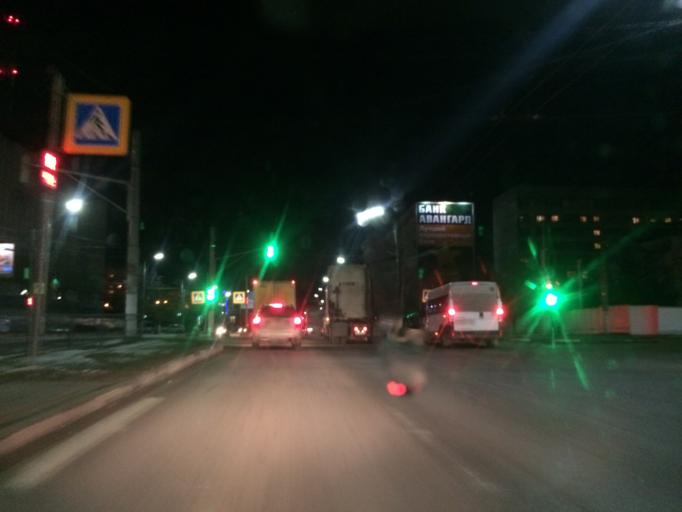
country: RU
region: Tula
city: Tula
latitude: 54.2011
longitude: 37.6466
